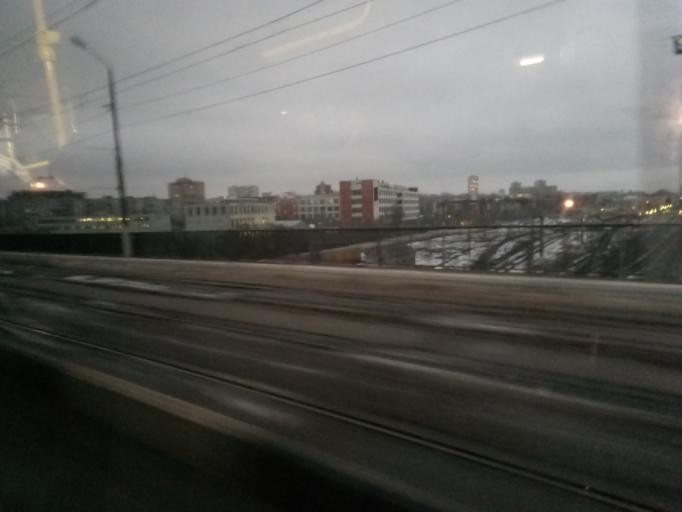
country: RU
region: Tula
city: Tula
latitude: 54.2047
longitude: 37.5831
